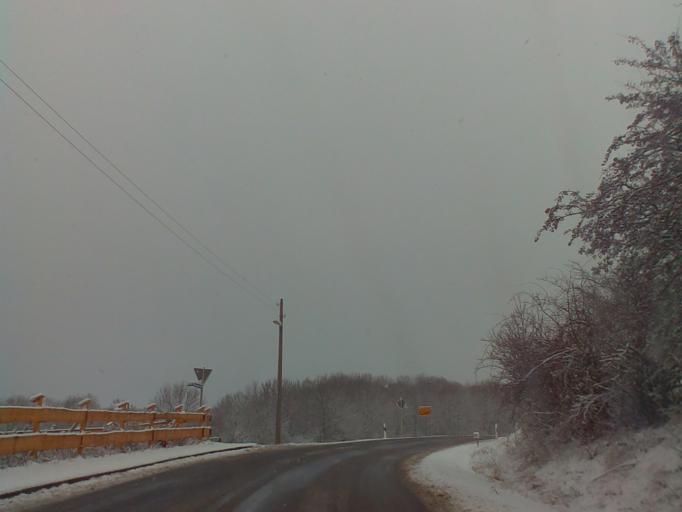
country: DE
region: Thuringia
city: Apfelstadt
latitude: 50.8521
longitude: 10.8787
